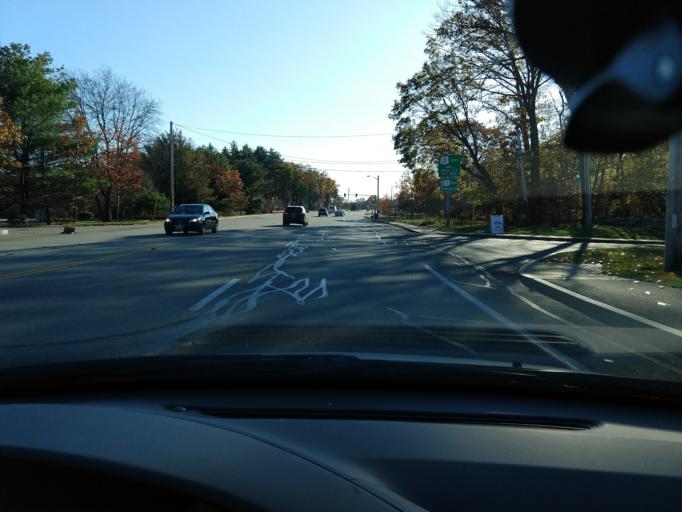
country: US
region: Massachusetts
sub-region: Middlesex County
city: Billerica
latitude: 42.5457
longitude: -71.2826
